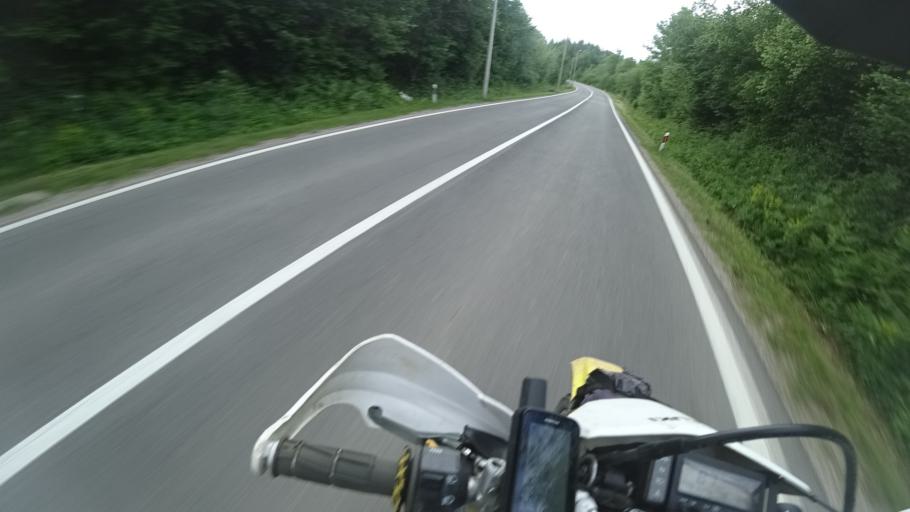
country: HR
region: Licko-Senjska
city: Gospic
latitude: 44.4937
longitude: 15.4600
